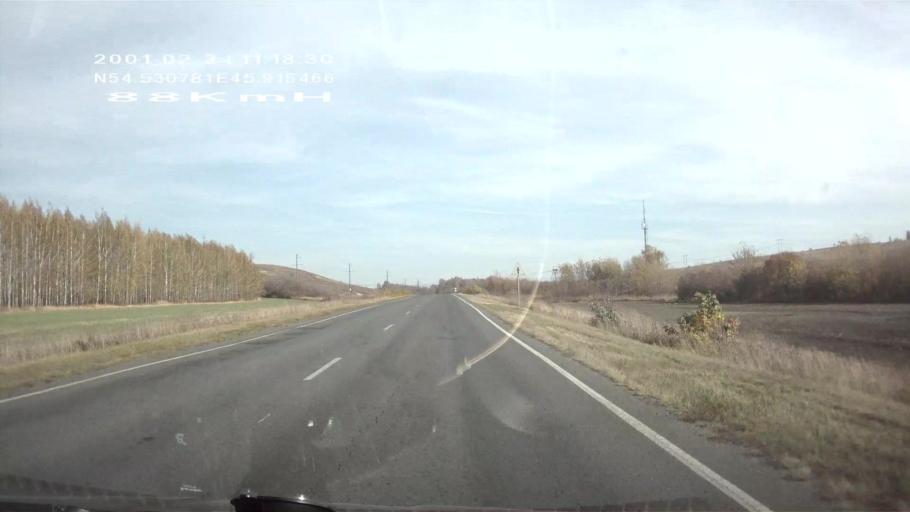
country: RU
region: Mordoviya
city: Atyashevo
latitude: 54.5308
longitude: 45.9157
